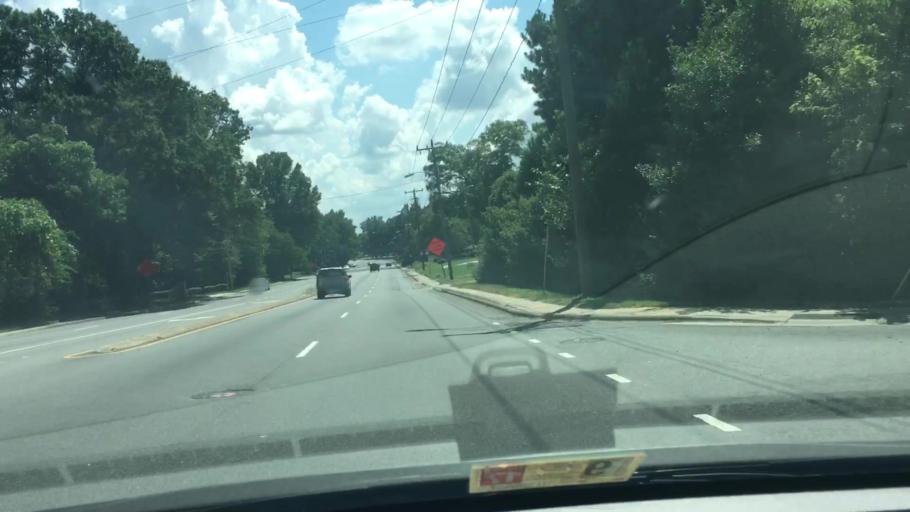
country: US
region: North Carolina
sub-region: Mecklenburg County
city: Charlotte
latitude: 35.2649
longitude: -80.7951
